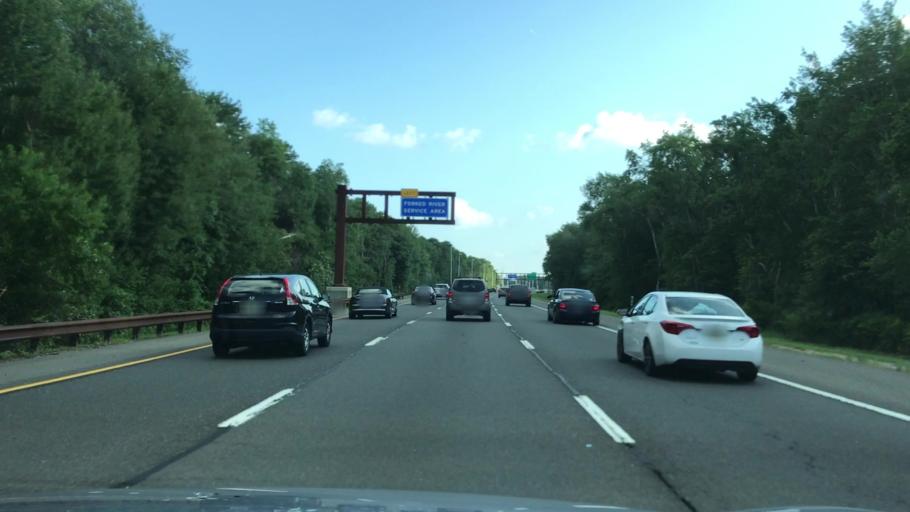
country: US
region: New Jersey
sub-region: Ocean County
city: Forked River
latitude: 39.8805
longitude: -74.2133
